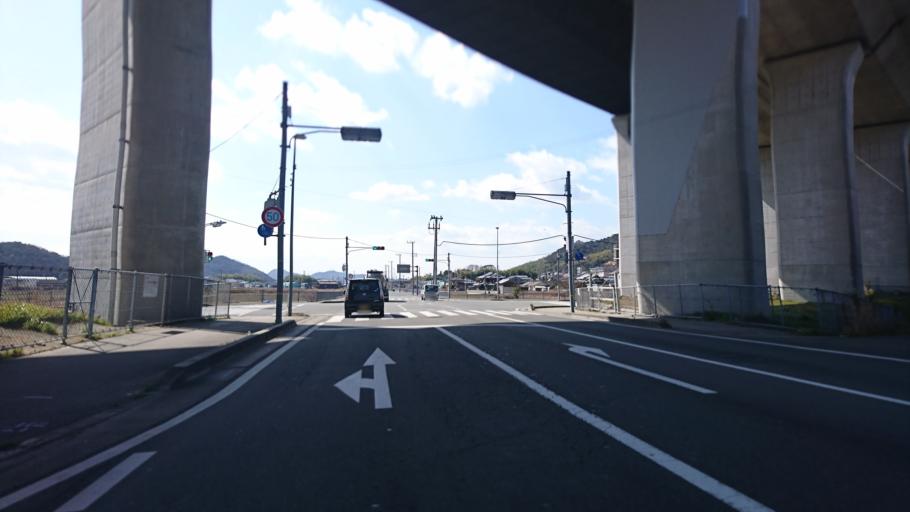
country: JP
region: Hyogo
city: Himeji
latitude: 34.8493
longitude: 134.7535
